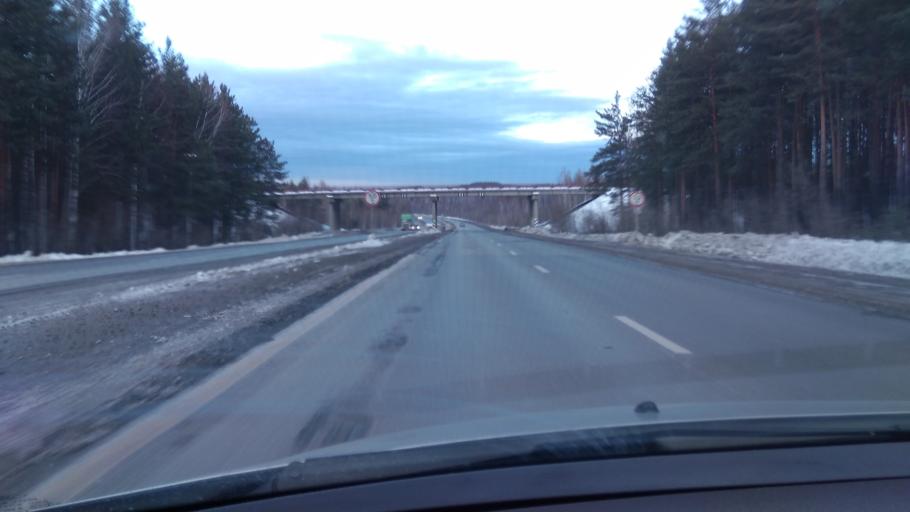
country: RU
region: Sverdlovsk
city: Shchelkun
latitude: 56.3168
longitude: 60.8692
